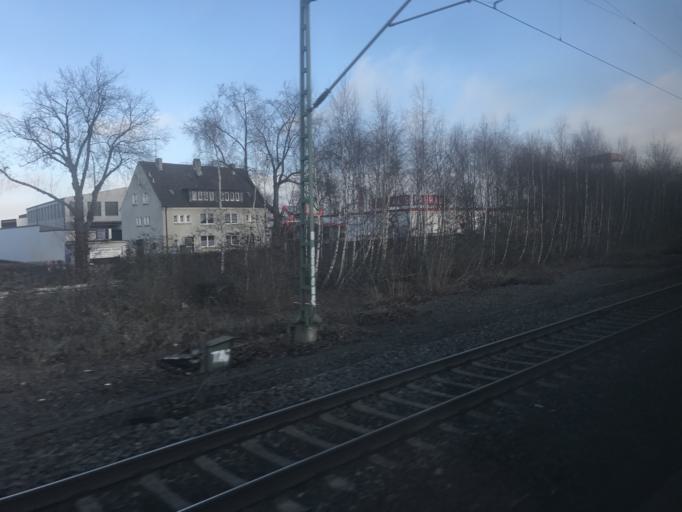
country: DE
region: North Rhine-Westphalia
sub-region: Regierungsbezirk Munster
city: Gelsenkirchen
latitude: 51.4728
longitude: 7.1343
